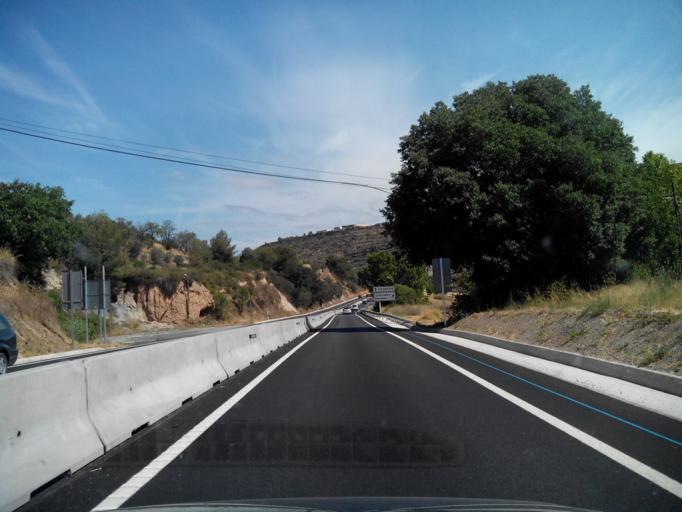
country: ES
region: Catalonia
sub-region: Provincia de Barcelona
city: Manresa
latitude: 41.6989
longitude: 1.8417
